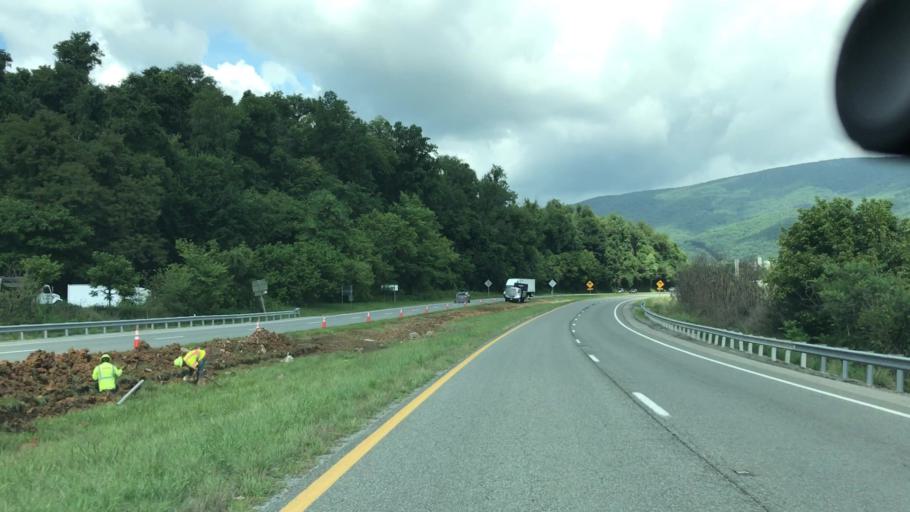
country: US
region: Virginia
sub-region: Giles County
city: Pearisburg
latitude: 37.3355
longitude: -80.7520
